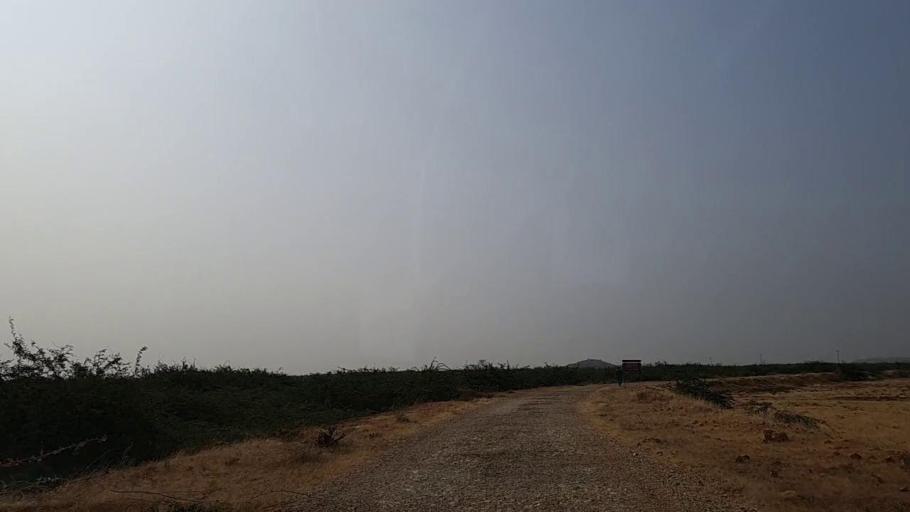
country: PK
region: Sindh
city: Thatta
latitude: 24.7222
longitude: 67.8320
